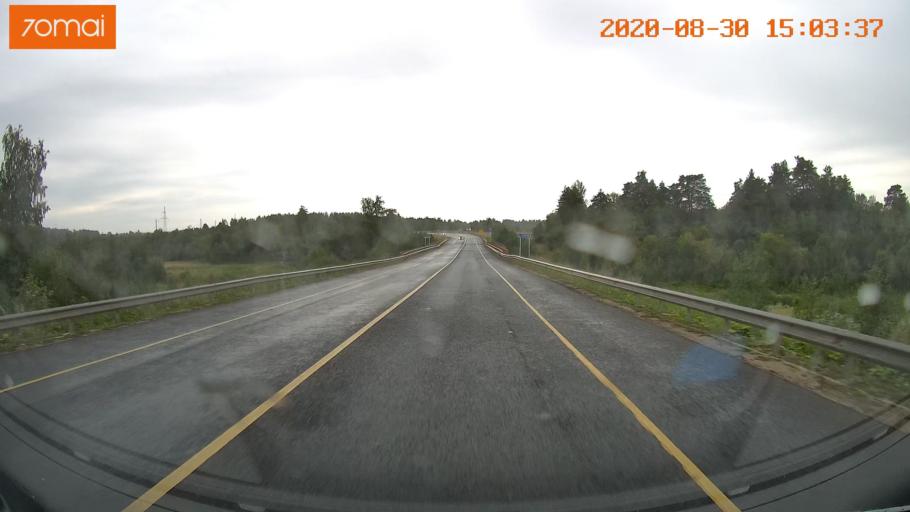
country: RU
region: Ivanovo
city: Staraya Vichuga
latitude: 57.2971
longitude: 41.9102
